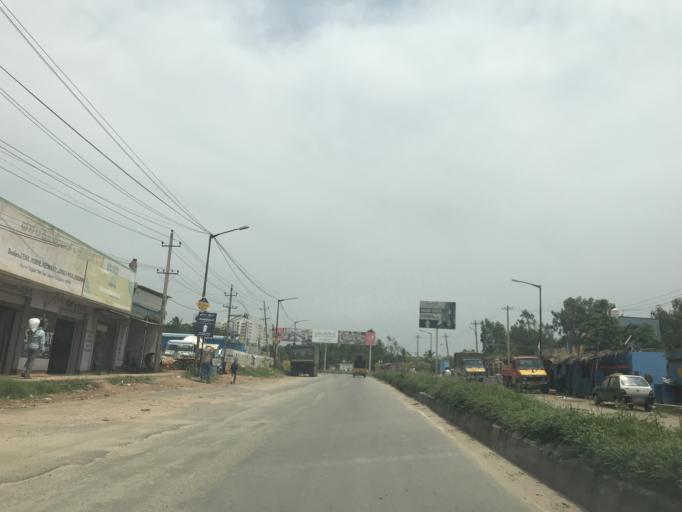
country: IN
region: Karnataka
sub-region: Bangalore Urban
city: Yelahanka
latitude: 13.0910
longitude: 77.6546
